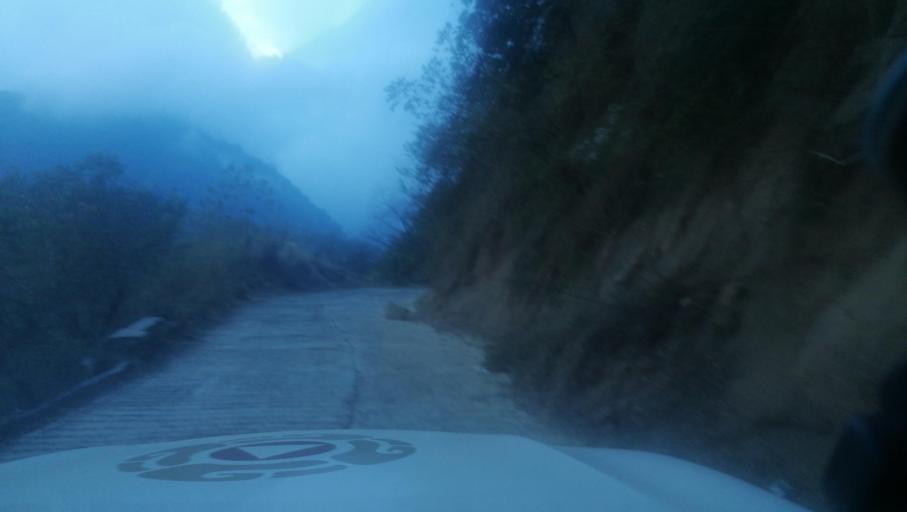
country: MX
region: Chiapas
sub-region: Cacahoatan
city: Benito Juarez
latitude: 15.1388
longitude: -92.1990
